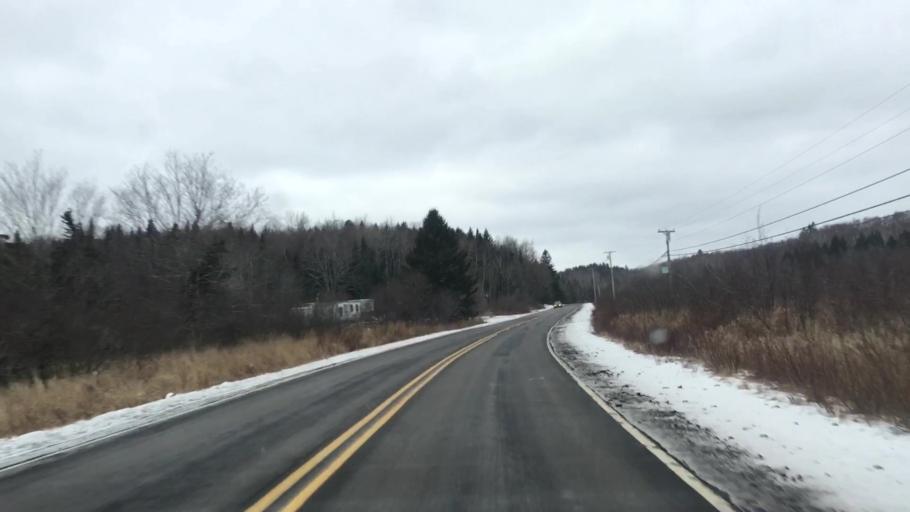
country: US
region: Maine
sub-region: Washington County
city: Machiasport
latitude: 44.7090
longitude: -67.3676
